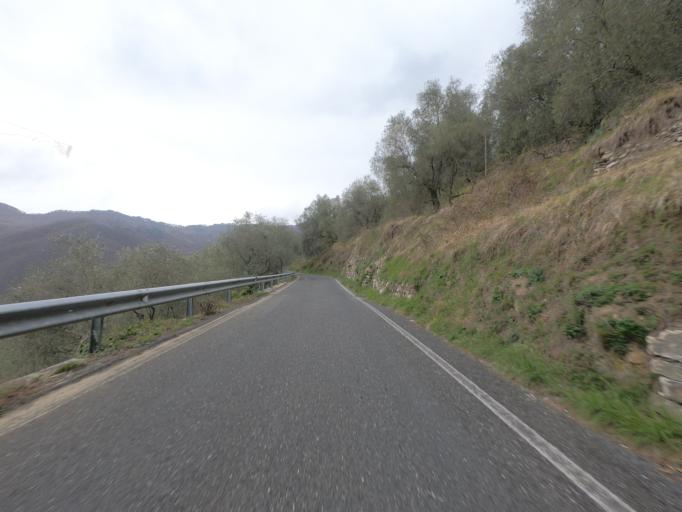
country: IT
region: Liguria
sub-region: Provincia di Savona
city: Testico
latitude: 44.0256
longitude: 8.0041
